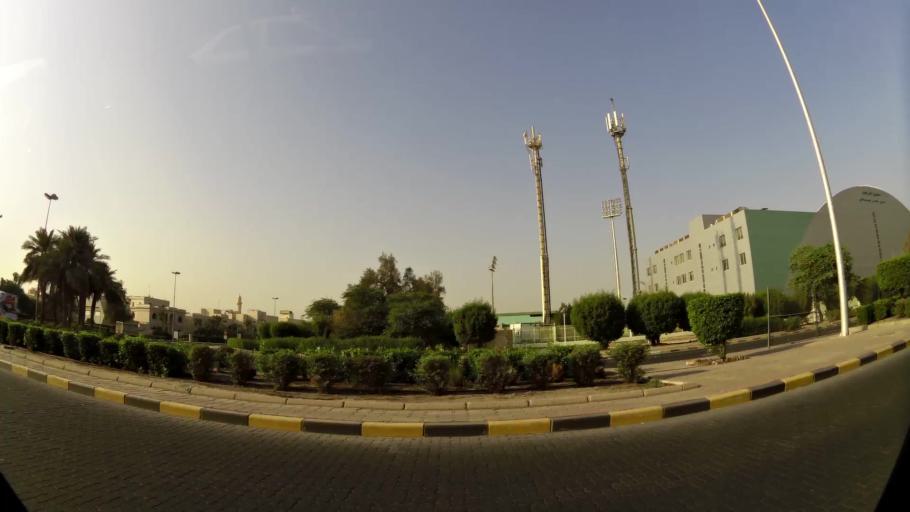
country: KW
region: Al Asimah
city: Ad Dasmah
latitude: 29.3575
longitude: 48.0027
